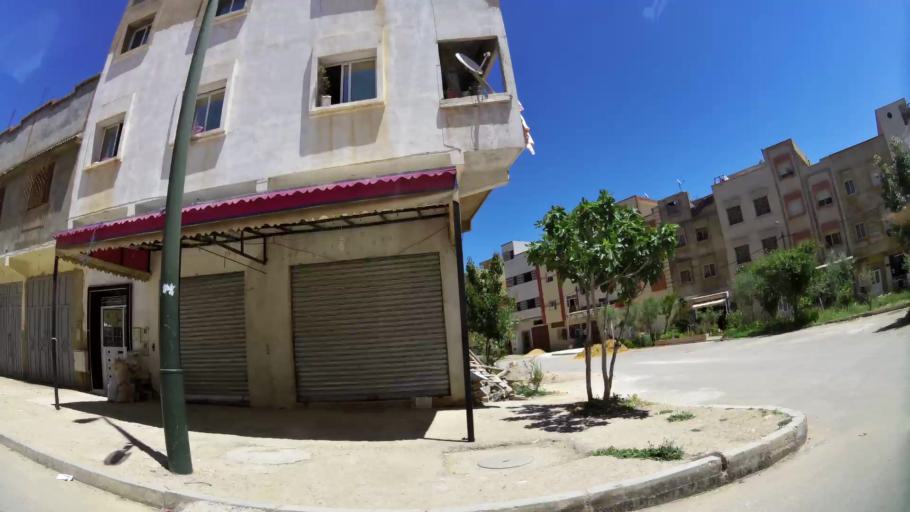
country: MA
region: Meknes-Tafilalet
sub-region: Meknes
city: Meknes
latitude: 33.8622
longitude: -5.5659
